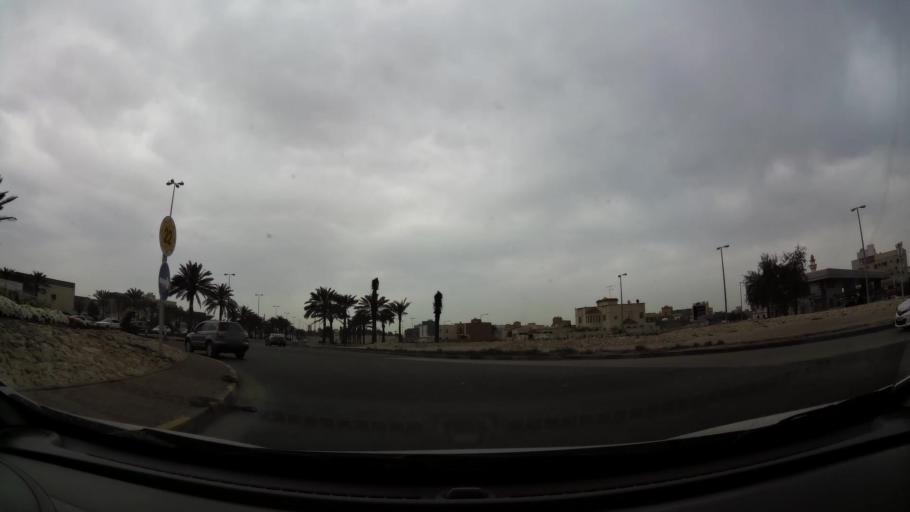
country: BH
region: Central Governorate
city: Dar Kulayb
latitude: 26.0629
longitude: 50.5074
